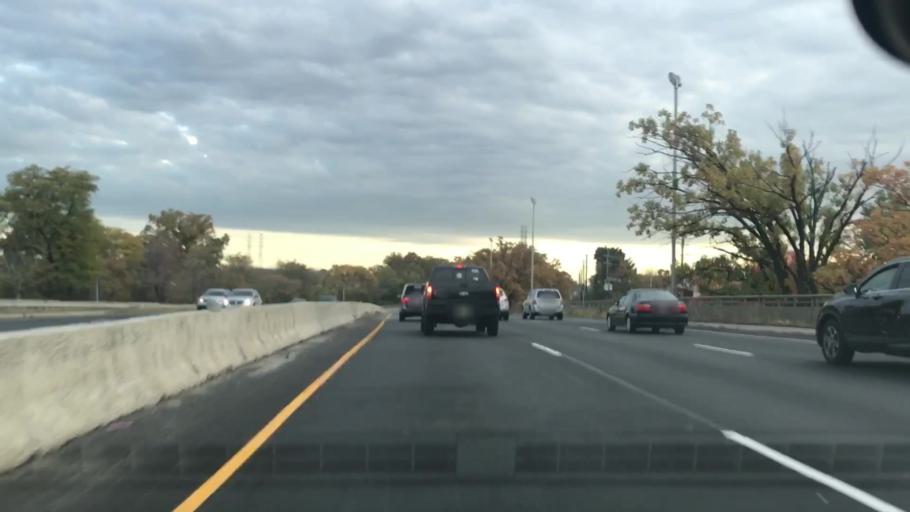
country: US
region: New Jersey
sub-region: Bergen County
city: Lyndhurst
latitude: 40.8112
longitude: -74.1396
